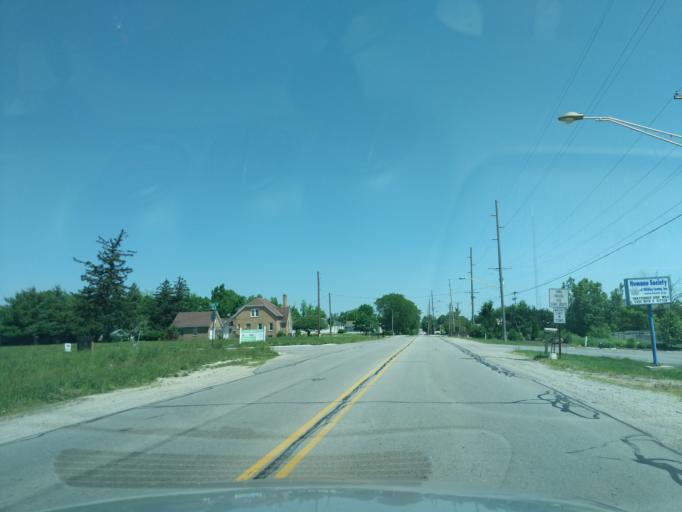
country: US
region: Indiana
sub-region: Whitley County
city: Columbia City
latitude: 41.1472
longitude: -85.4912
